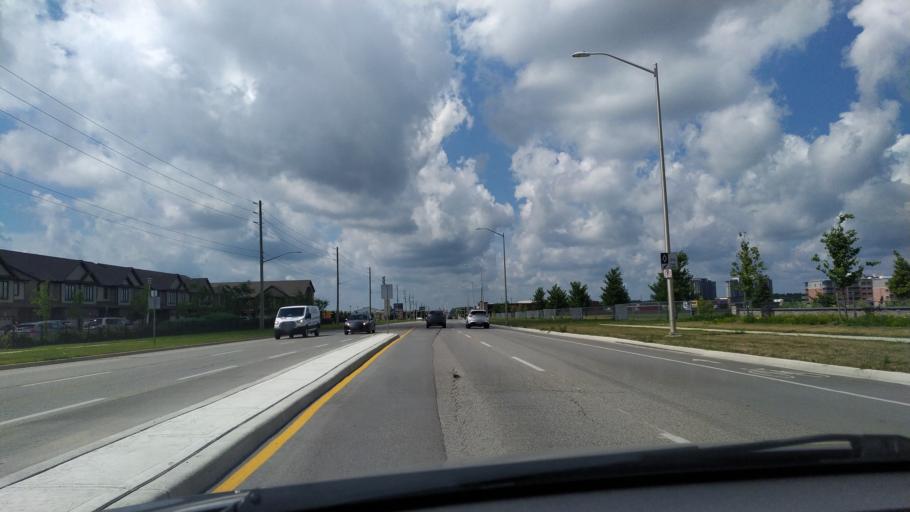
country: CA
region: Ontario
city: London
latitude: 43.0140
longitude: -81.3261
